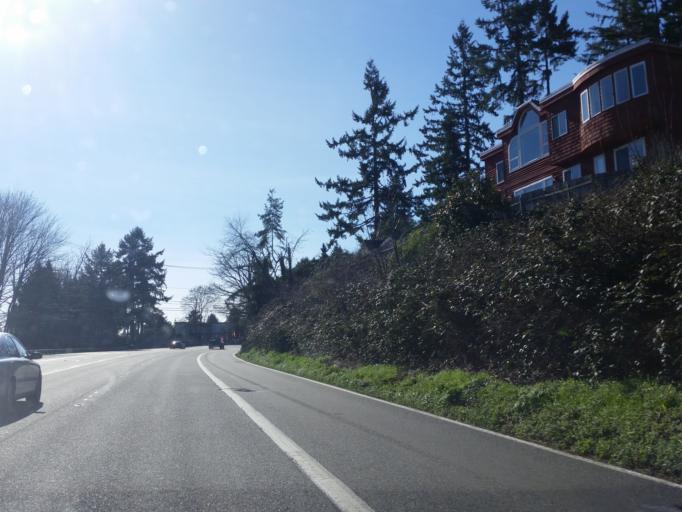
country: US
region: Washington
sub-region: King County
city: Lake Forest Park
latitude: 47.7441
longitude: -122.2867
